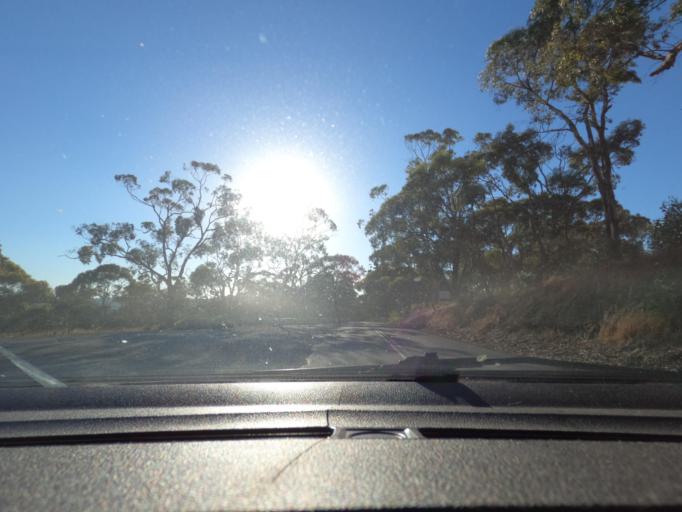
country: AU
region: South Australia
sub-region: Clare and Gilbert Valleys
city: Clare
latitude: -33.9054
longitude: 138.6587
